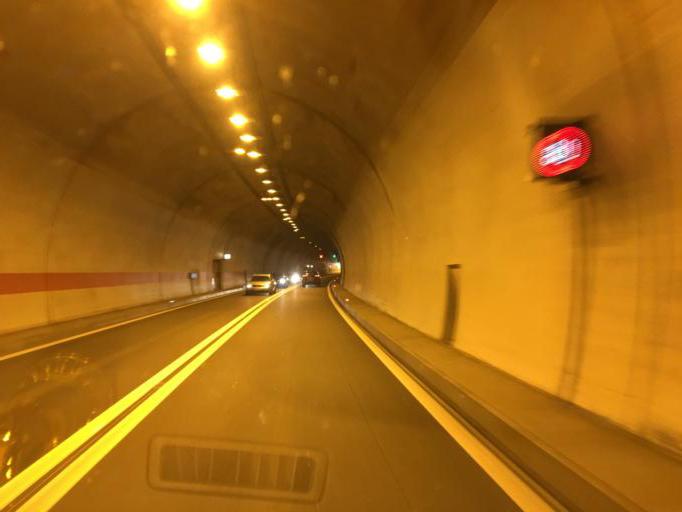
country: HR
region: Krapinsko-Zagorska
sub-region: Grad Krapina
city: Krapina
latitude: 46.1842
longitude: 15.8461
